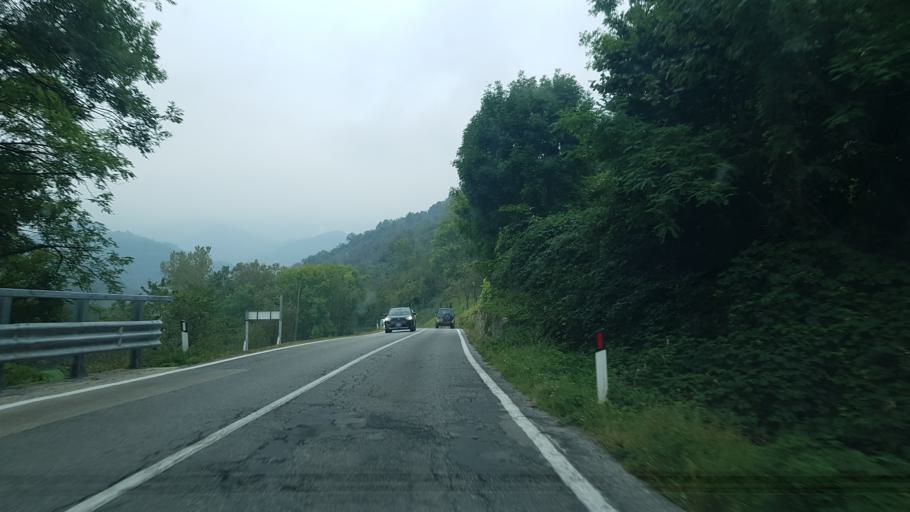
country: IT
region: Piedmont
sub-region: Provincia di Cuneo
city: Frabosa Sottana
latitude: 44.3137
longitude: 7.8036
